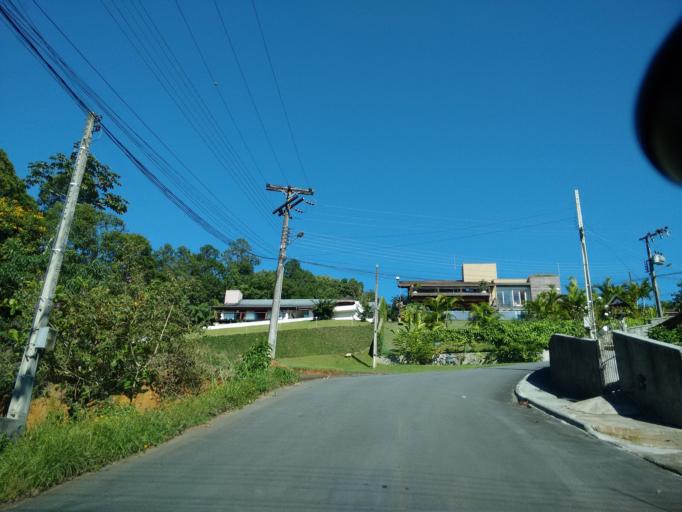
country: BR
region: Santa Catarina
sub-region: Pomerode
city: Pomerode
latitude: -26.7319
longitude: -49.1816
